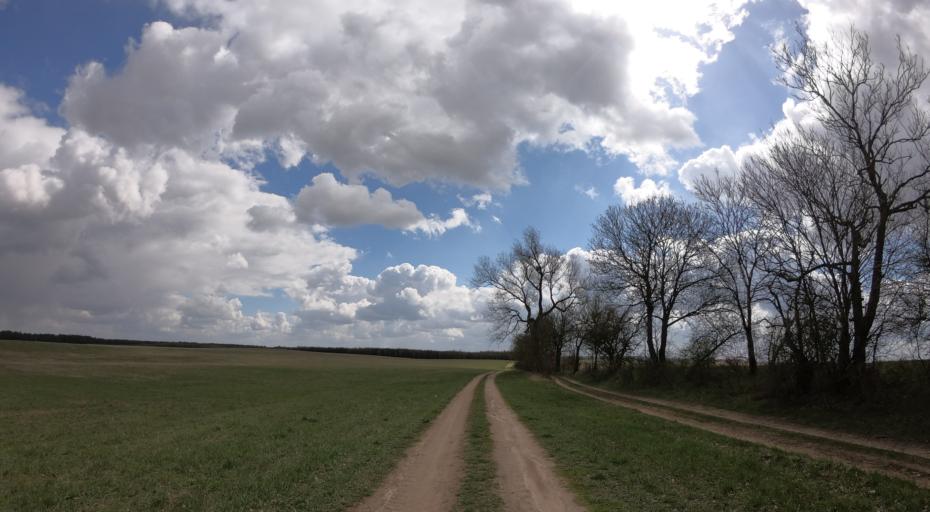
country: PL
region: West Pomeranian Voivodeship
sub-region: Powiat drawski
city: Drawsko Pomorskie
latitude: 53.5590
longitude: 15.8556
